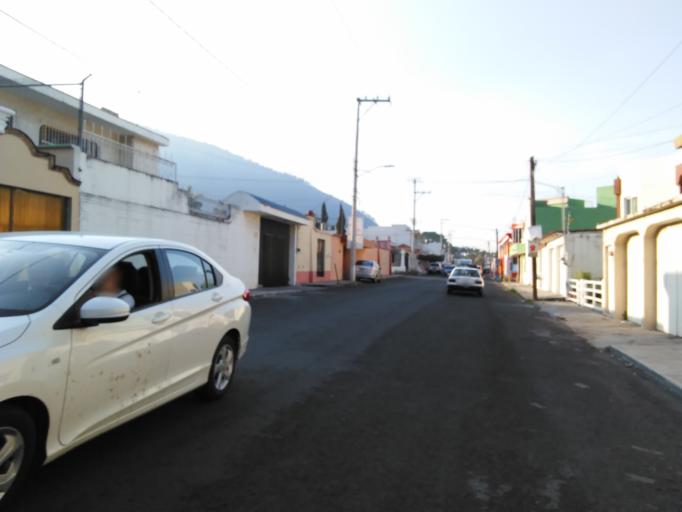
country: MX
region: Nayarit
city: Tepic
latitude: 21.5045
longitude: -104.9097
